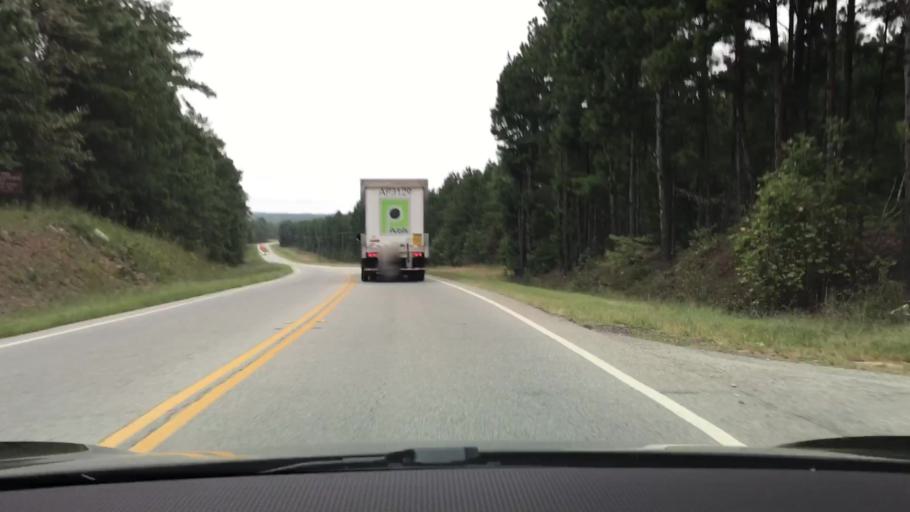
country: US
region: Georgia
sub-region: Greene County
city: Greensboro
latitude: 33.6641
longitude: -83.2458
